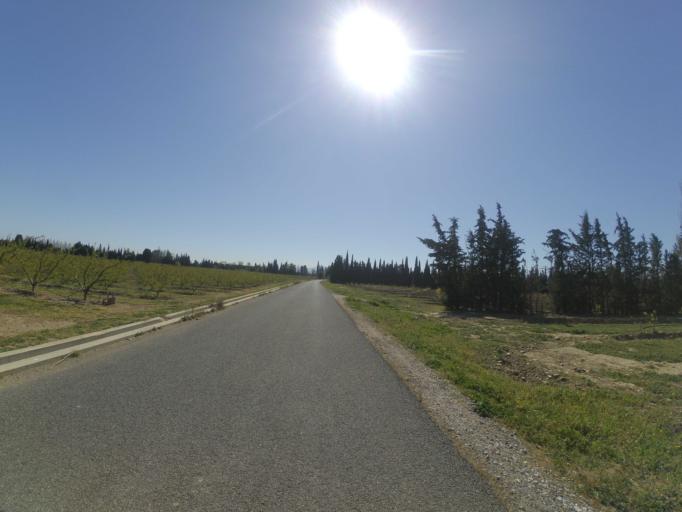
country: FR
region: Languedoc-Roussillon
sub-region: Departement des Pyrenees-Orientales
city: Corneilla-la-Riviere
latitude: 42.6783
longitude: 2.7245
